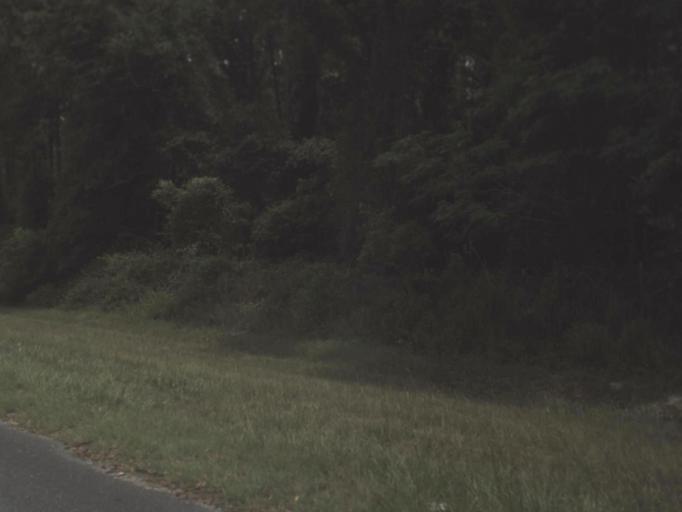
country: US
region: Florida
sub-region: Taylor County
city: Perry
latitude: 30.0811
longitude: -83.5114
